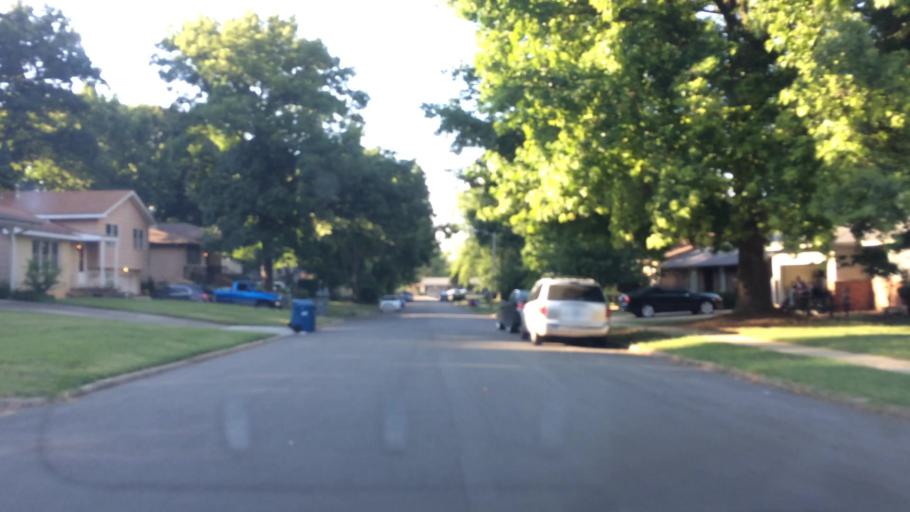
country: US
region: Missouri
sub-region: Greene County
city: Springfield
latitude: 37.2016
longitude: -93.2566
